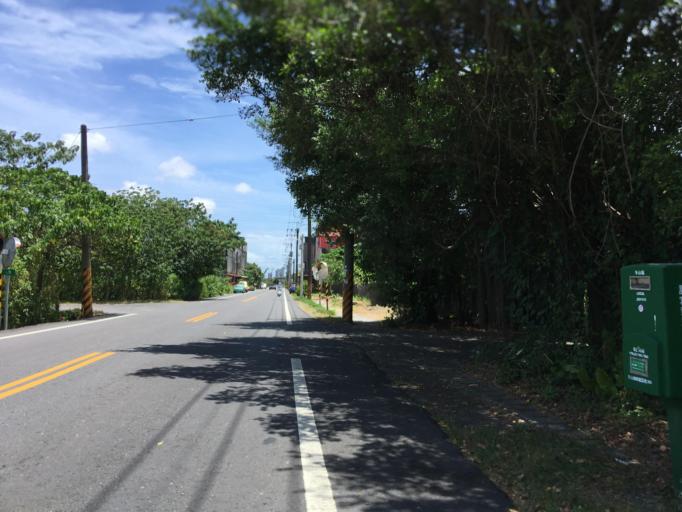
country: TW
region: Taiwan
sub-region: Yilan
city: Yilan
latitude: 24.6615
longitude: 121.7369
